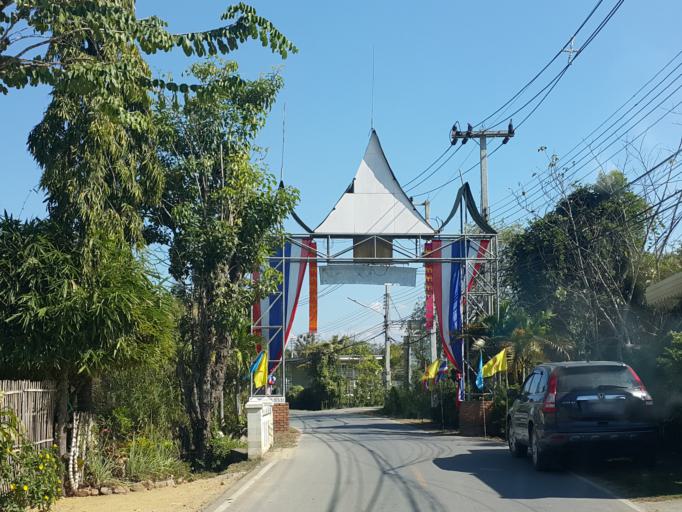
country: TH
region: Chiang Mai
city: San Sai
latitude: 18.8749
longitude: 99.0082
